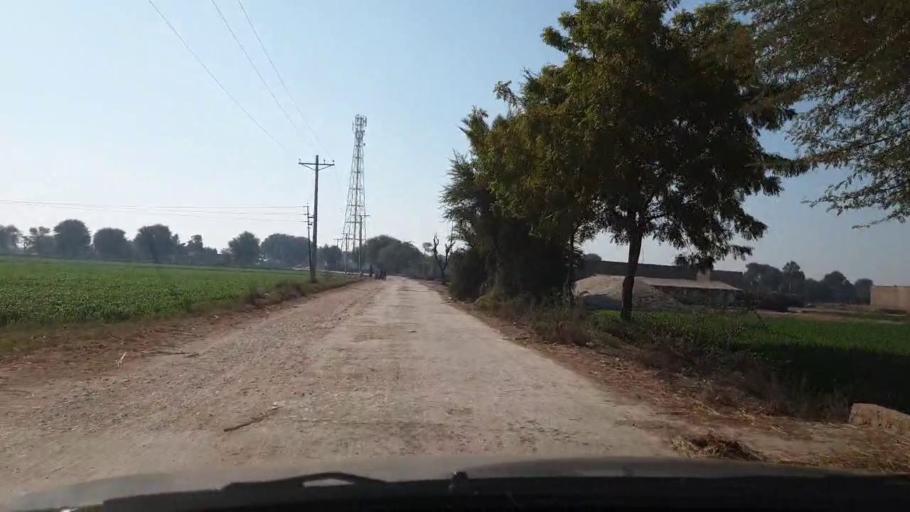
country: PK
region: Sindh
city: Jhol
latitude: 25.9410
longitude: 68.8200
